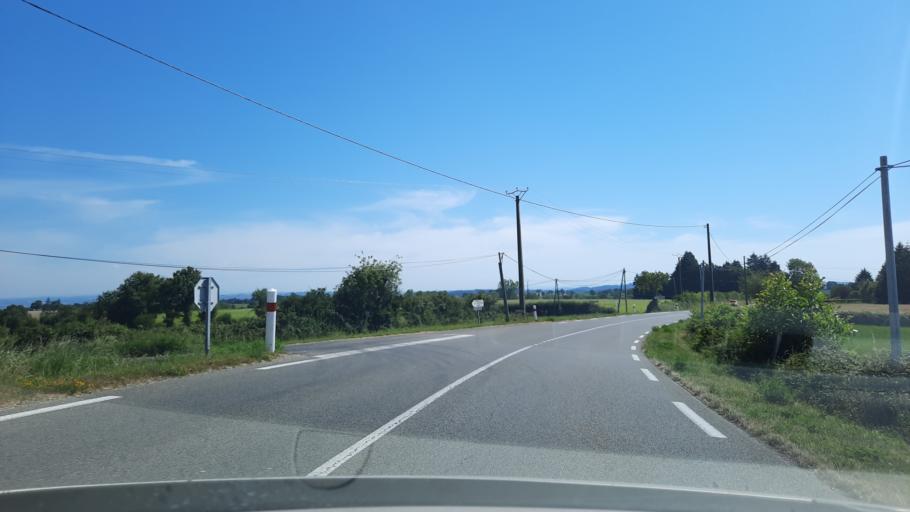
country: FR
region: Midi-Pyrenees
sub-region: Departement de l'Aveyron
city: Montbazens
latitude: 44.4428
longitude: 2.1978
